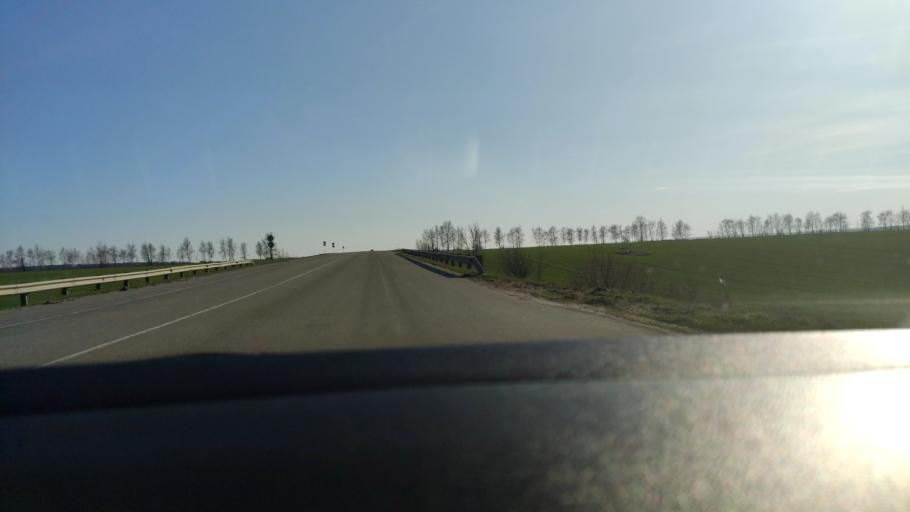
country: RU
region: Voronezj
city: Kolodeznyy
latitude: 51.3965
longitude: 39.2344
